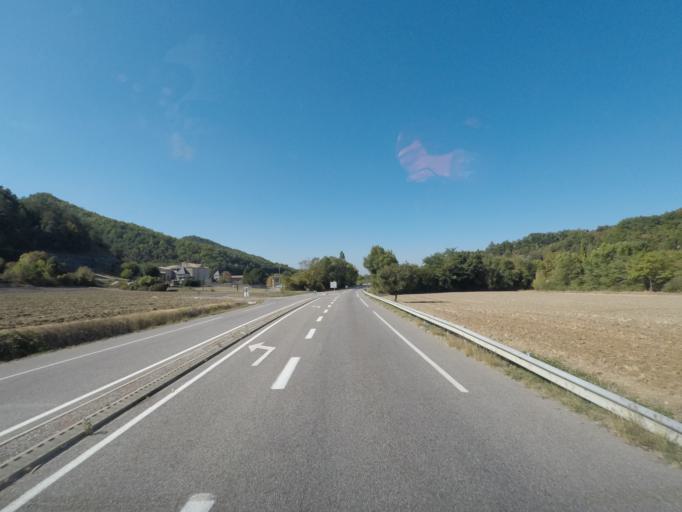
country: FR
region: Rhone-Alpes
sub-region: Departement de la Drome
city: Aouste-sur-Sye
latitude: 44.6927
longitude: 5.1768
